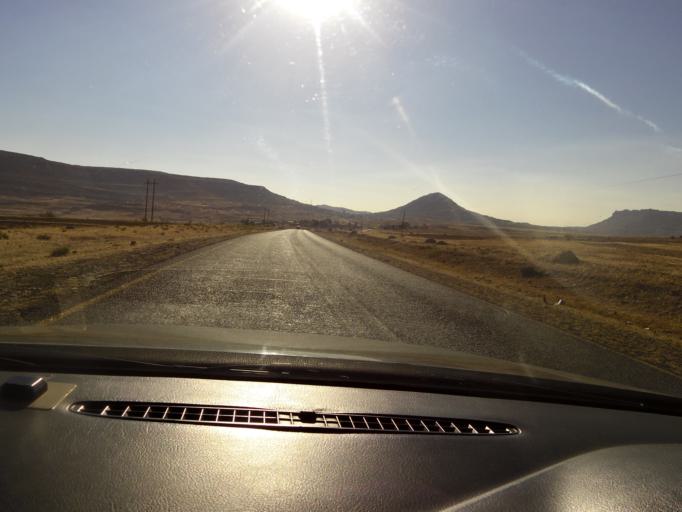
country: LS
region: Mafeteng
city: Mafeteng
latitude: -29.9711
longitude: 27.3104
